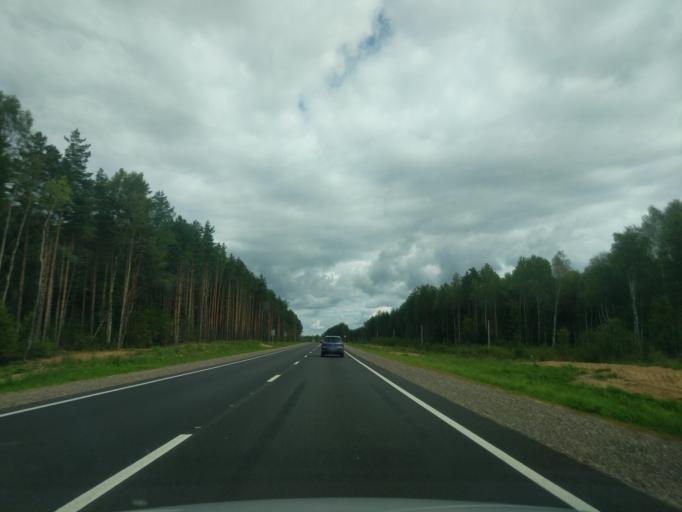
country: RU
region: Jaroslavl
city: Tunoshna
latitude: 57.5686
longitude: 40.2625
